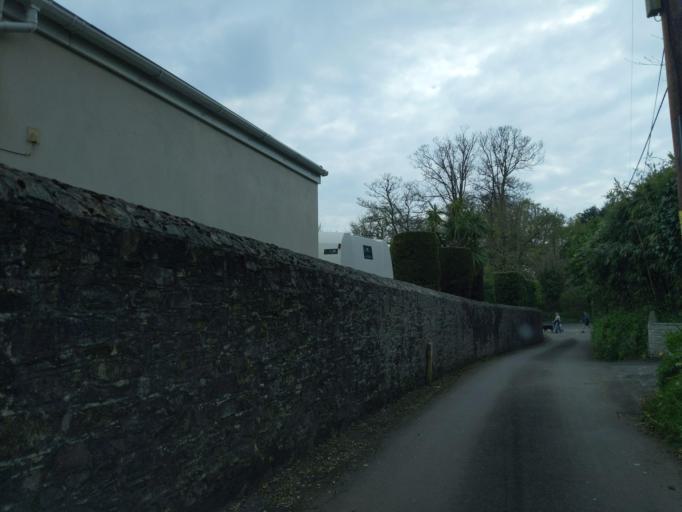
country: GB
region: England
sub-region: Devon
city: Yealmpton
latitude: 50.3505
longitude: -4.0419
